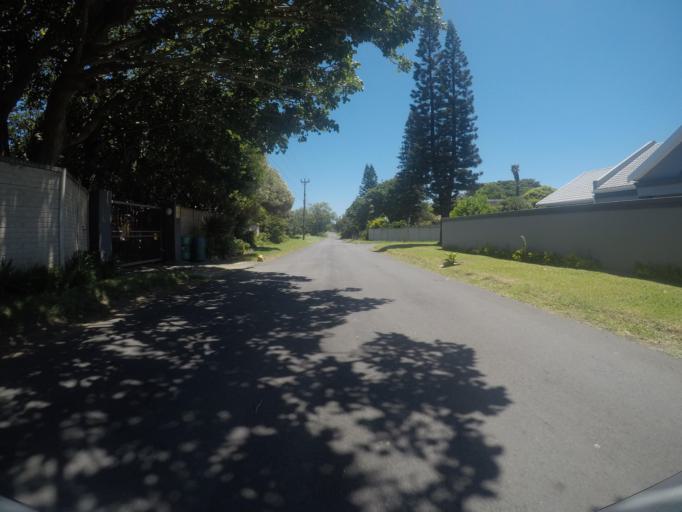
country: ZA
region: Eastern Cape
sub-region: Buffalo City Metropolitan Municipality
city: East London
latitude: -32.9560
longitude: 27.9993
